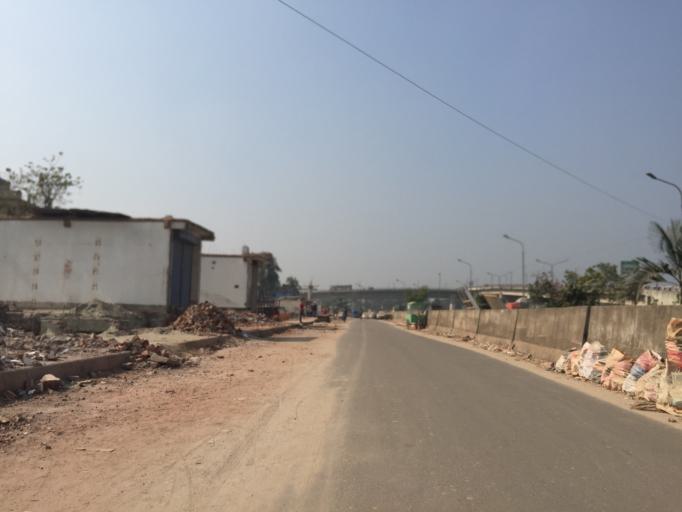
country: BD
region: Dhaka
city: Tungi
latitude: 23.8251
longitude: 90.4238
